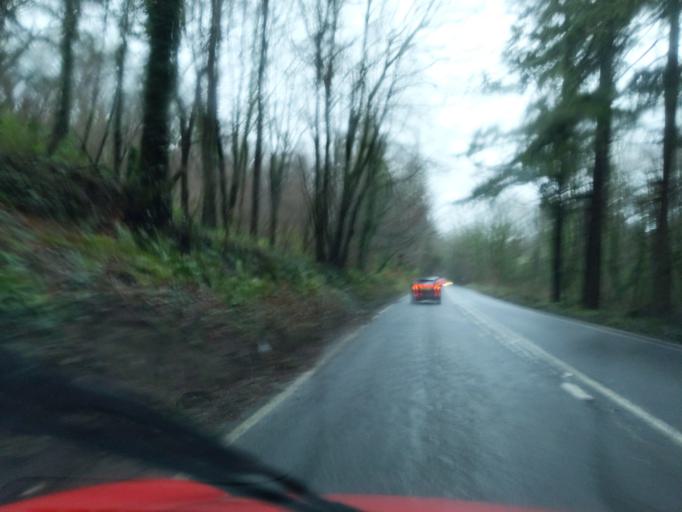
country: GB
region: England
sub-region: Cornwall
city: South Hill
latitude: 50.5586
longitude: -4.3303
